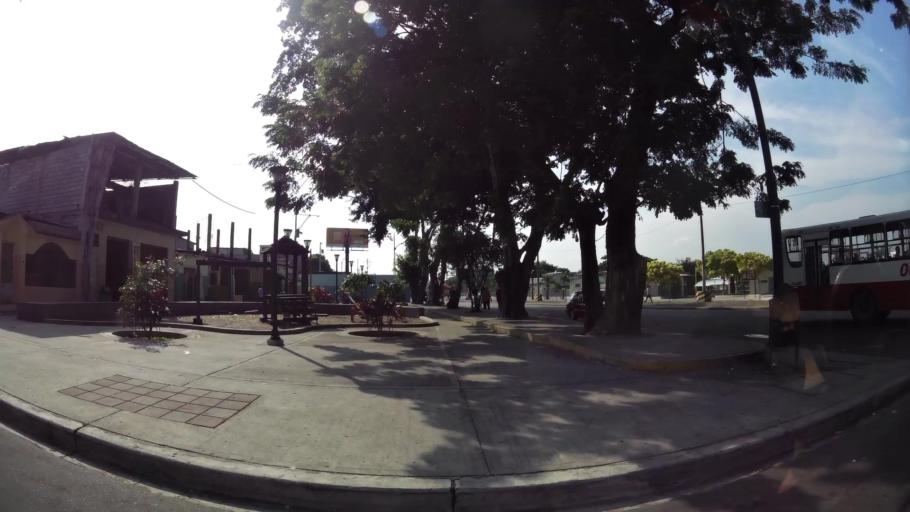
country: EC
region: Guayas
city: Guayaquil
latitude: -2.1880
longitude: -79.9084
